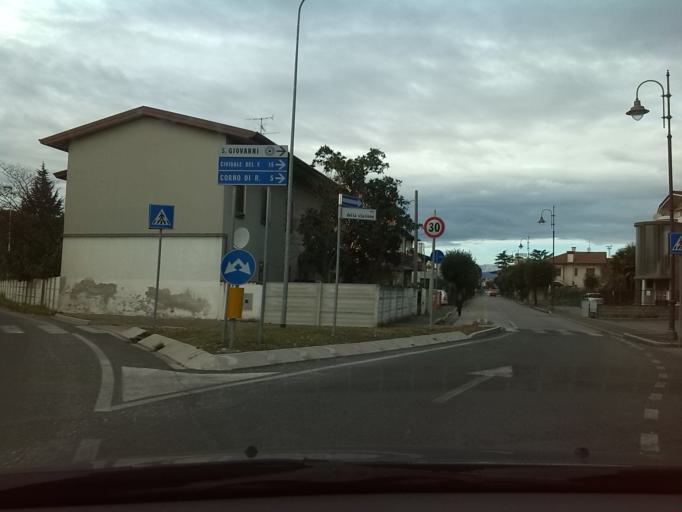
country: IT
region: Friuli Venezia Giulia
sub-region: Provincia di Udine
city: San Giovanni al Natisone
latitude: 45.9730
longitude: 13.3975
